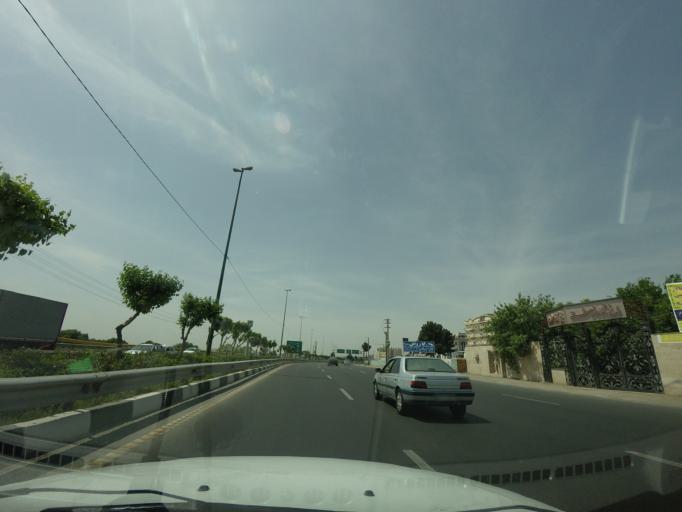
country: IR
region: Tehran
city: Eslamshahr
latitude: 35.5408
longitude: 51.2518
